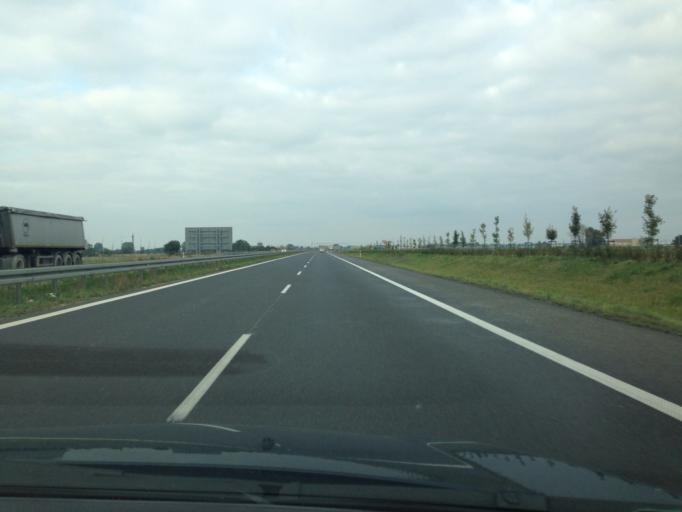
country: PL
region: Greater Poland Voivodeship
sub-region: Powiat poznanski
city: Kleszczewo
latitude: 52.3302
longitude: 17.1484
